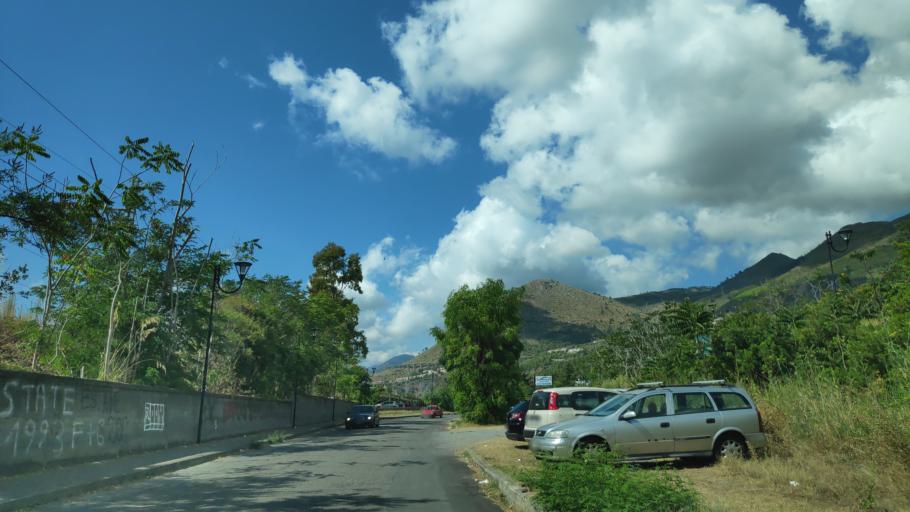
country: IT
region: Calabria
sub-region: Provincia di Cosenza
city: Praia a Mare
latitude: 39.8747
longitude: 15.7877
